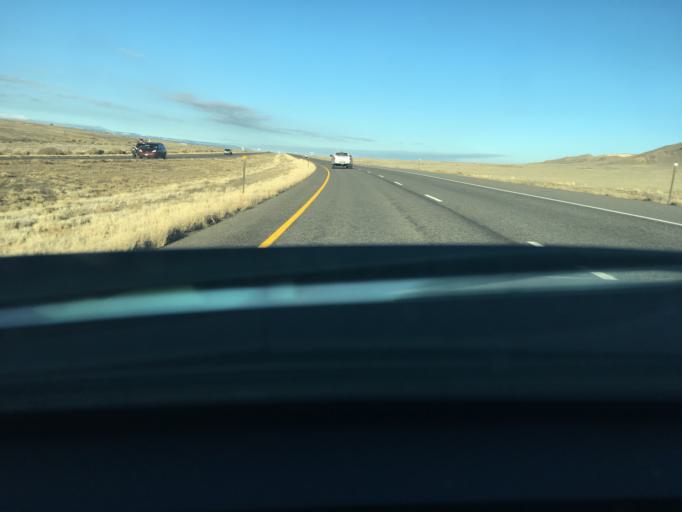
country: US
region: Colorado
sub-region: Delta County
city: Delta
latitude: 38.7771
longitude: -108.2323
